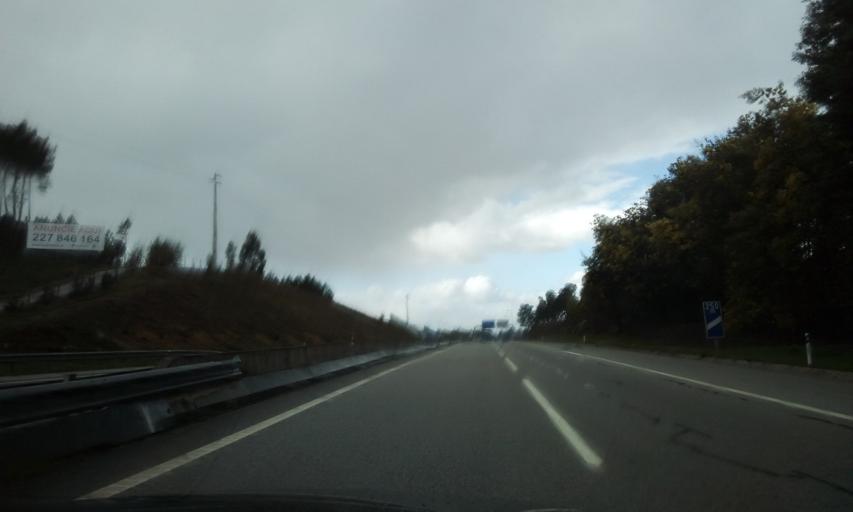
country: PT
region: Viseu
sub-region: Mangualde
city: Mangualde
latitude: 40.6161
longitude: -7.7542
